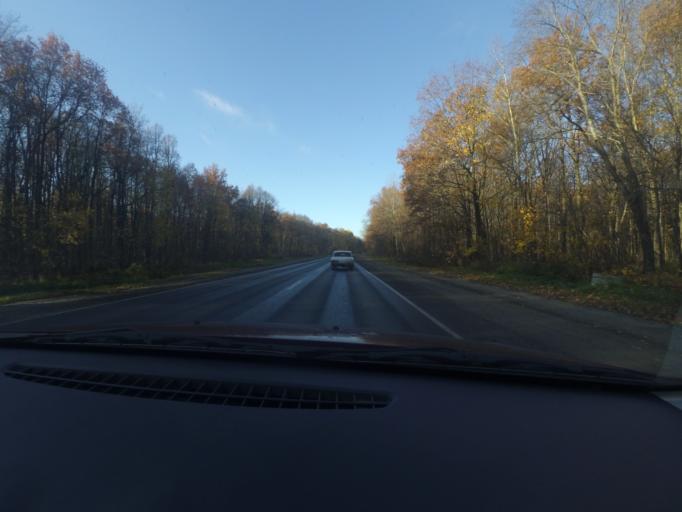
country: RU
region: Nizjnij Novgorod
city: Afonino
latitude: 56.2113
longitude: 44.0174
